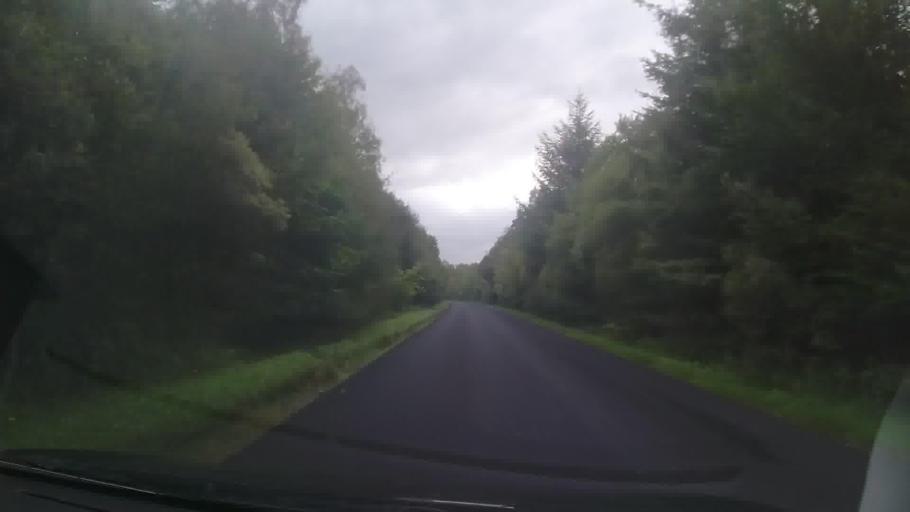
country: GB
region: Scotland
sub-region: Argyll and Bute
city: Garelochhead
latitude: 56.2359
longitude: -4.9666
